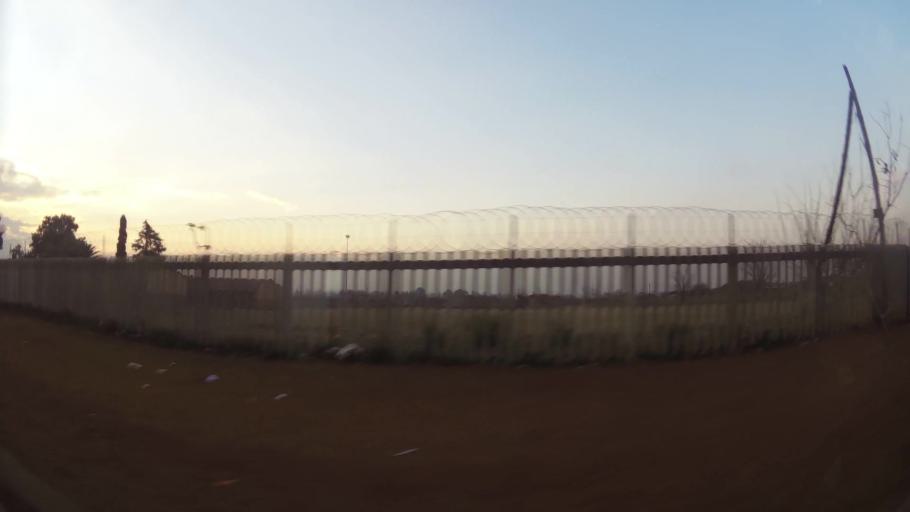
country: ZA
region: Gauteng
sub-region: City of Johannesburg Metropolitan Municipality
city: Orange Farm
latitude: -26.5541
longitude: 27.8655
